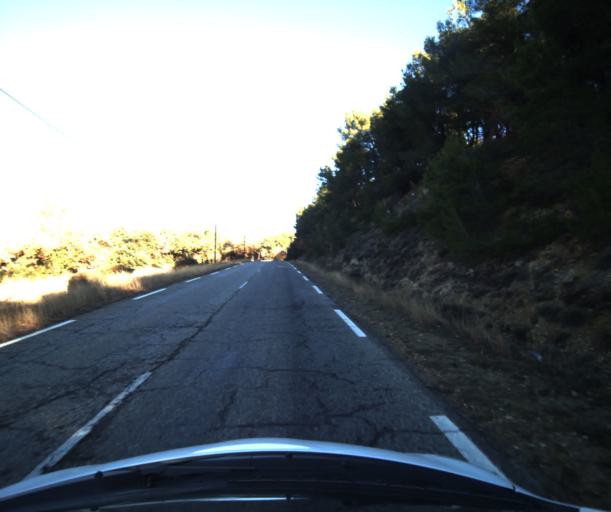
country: FR
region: Provence-Alpes-Cote d'Azur
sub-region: Departement du Vaucluse
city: Pertuis
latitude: 43.7208
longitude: 5.4992
